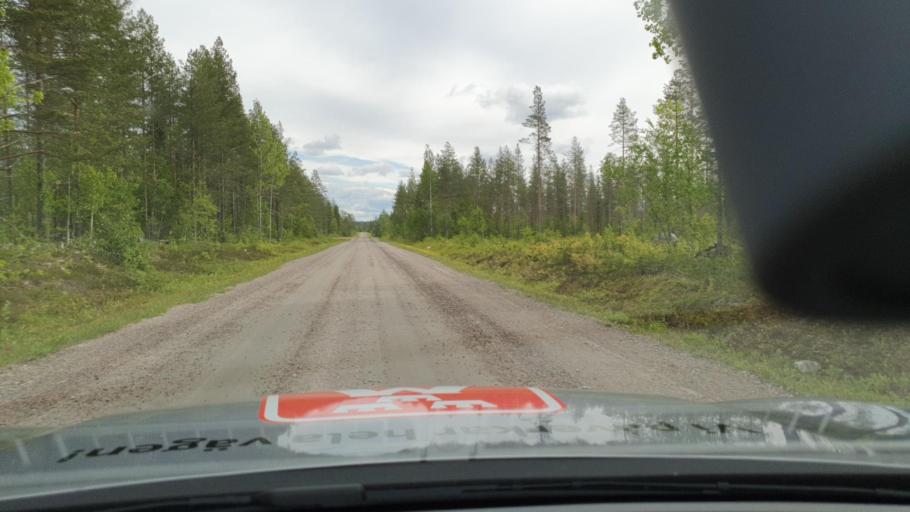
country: FI
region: Lapland
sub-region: Torniolaakso
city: Ylitornio
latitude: 65.9603
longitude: 23.6326
